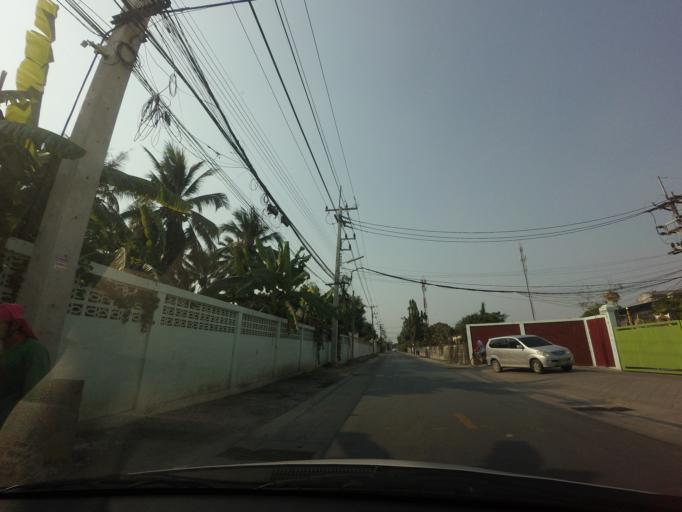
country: TH
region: Nakhon Pathom
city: Sam Phran
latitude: 13.6974
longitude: 100.2453
